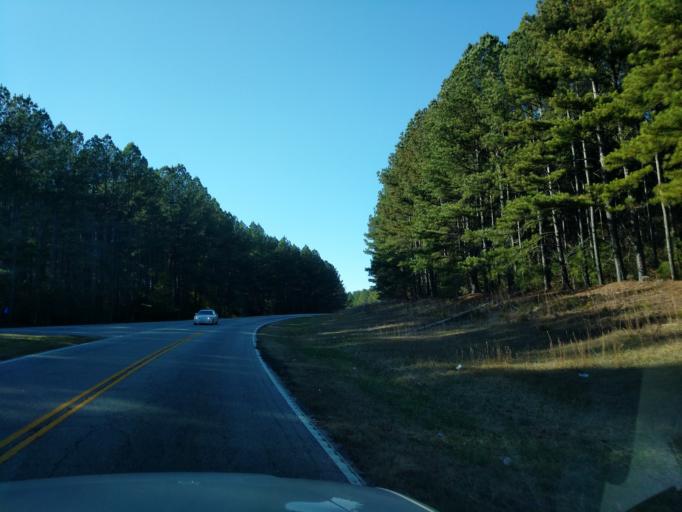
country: US
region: South Carolina
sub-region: Spartanburg County
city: Landrum
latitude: 35.1261
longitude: -82.1288
